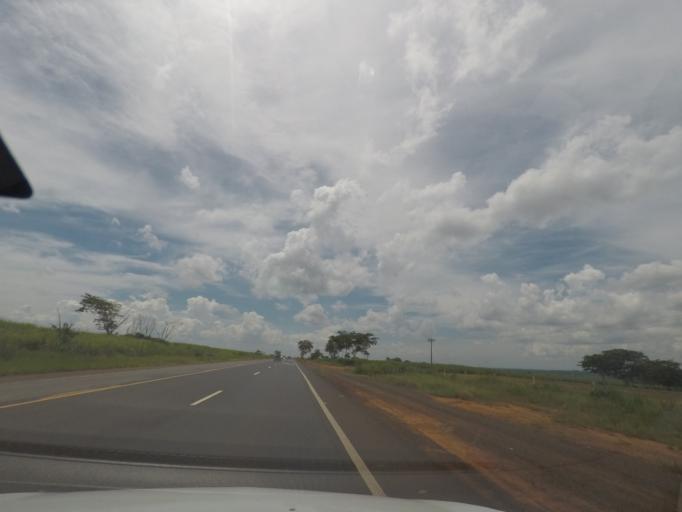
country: BR
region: Sao Paulo
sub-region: Barretos
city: Barretos
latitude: -20.3929
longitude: -48.6390
